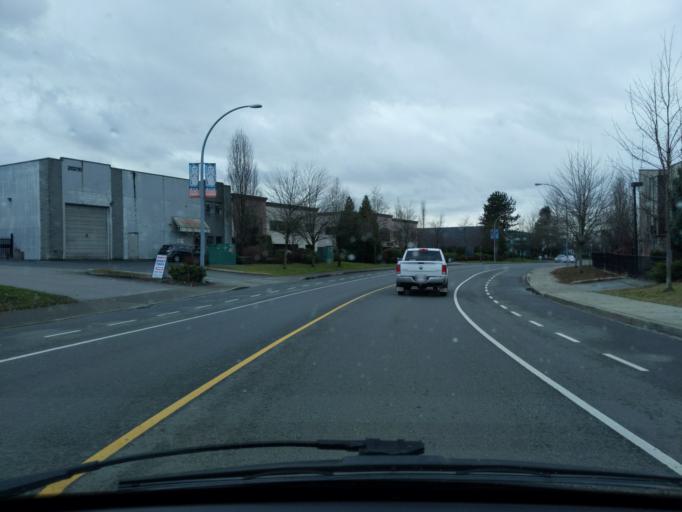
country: CA
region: British Columbia
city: Pitt Meadows
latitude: 49.2095
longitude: -122.6606
